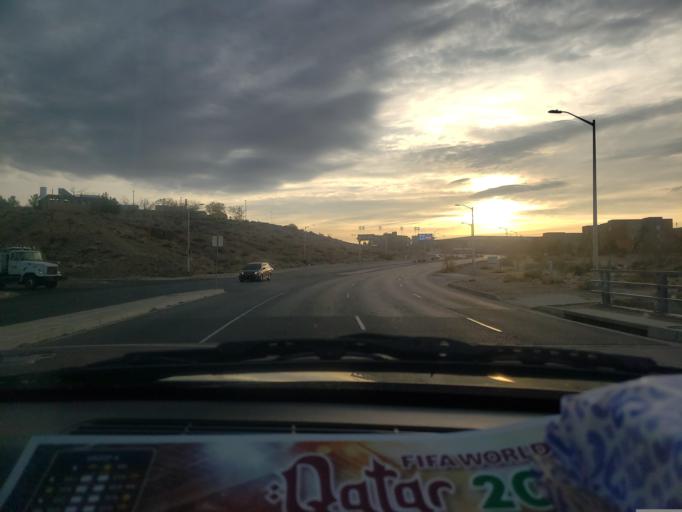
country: US
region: New Mexico
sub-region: Bernalillo County
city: Albuquerque
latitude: 35.0698
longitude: -106.6375
